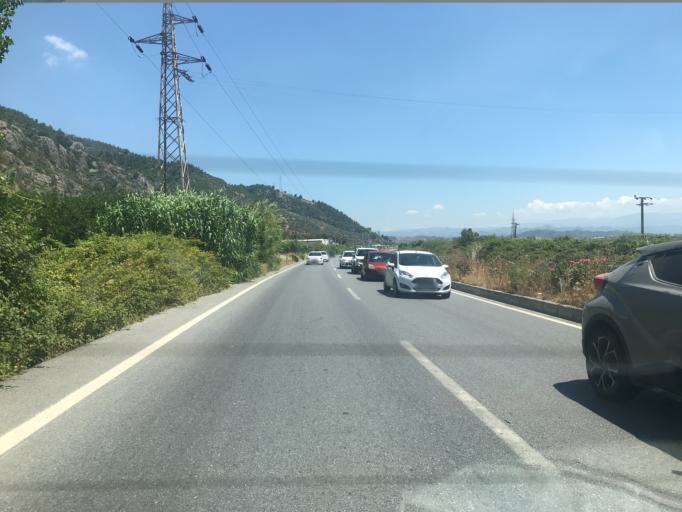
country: TR
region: Aydin
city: Soeke
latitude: 37.7950
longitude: 27.4671
